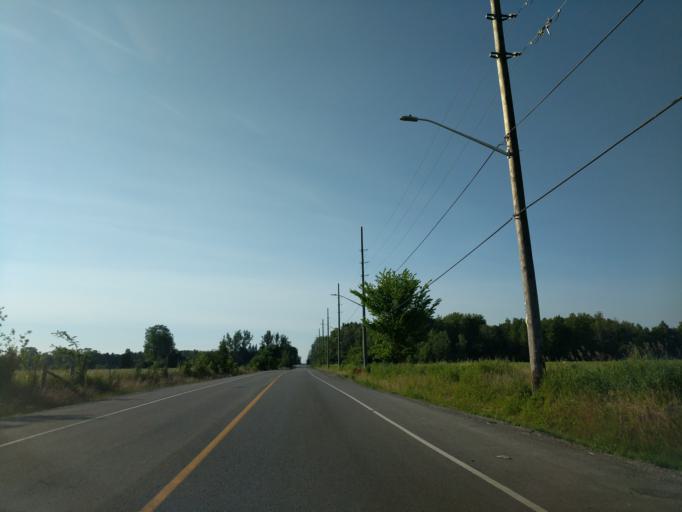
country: CA
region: Ontario
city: Oshawa
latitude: 43.9309
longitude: -78.9101
